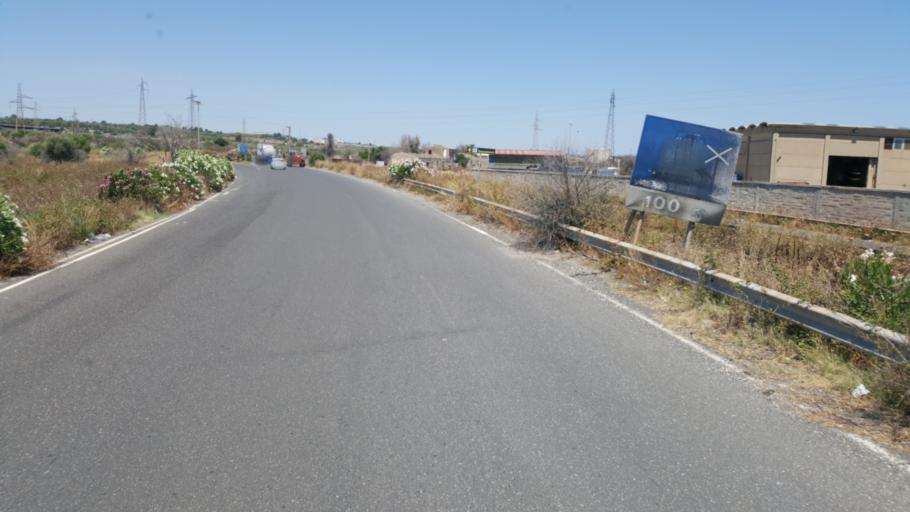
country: IT
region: Sicily
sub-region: Provincia di Siracusa
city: Melilli
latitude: 37.2020
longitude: 15.1632
